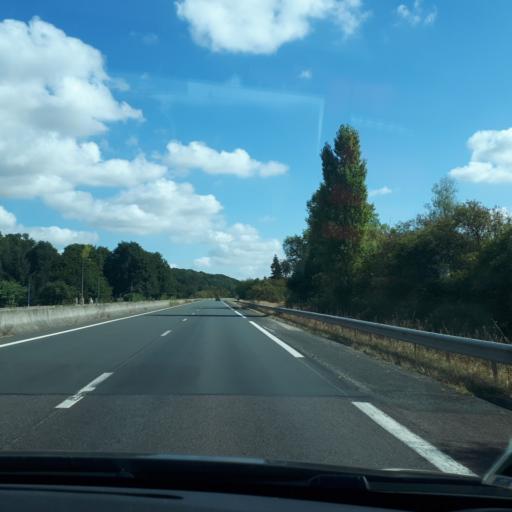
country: FR
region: Centre
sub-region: Departement du Loir-et-Cher
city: Moree
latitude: 47.8817
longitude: 1.1648
